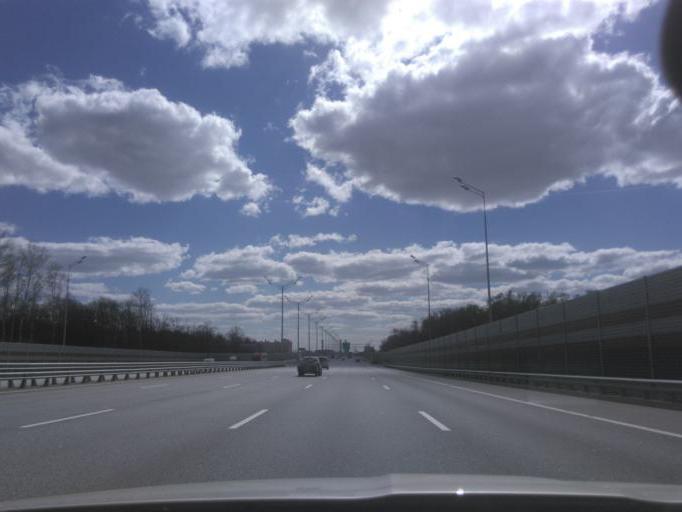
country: RU
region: Moscow
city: Khimki
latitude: 55.9151
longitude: 37.4614
